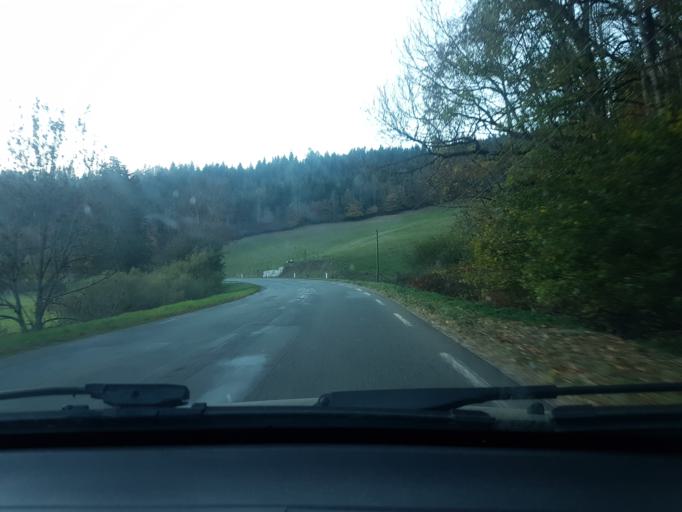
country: FR
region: Franche-Comte
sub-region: Departement du Doubs
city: Villers-le-Lac
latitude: 47.0539
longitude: 6.6604
